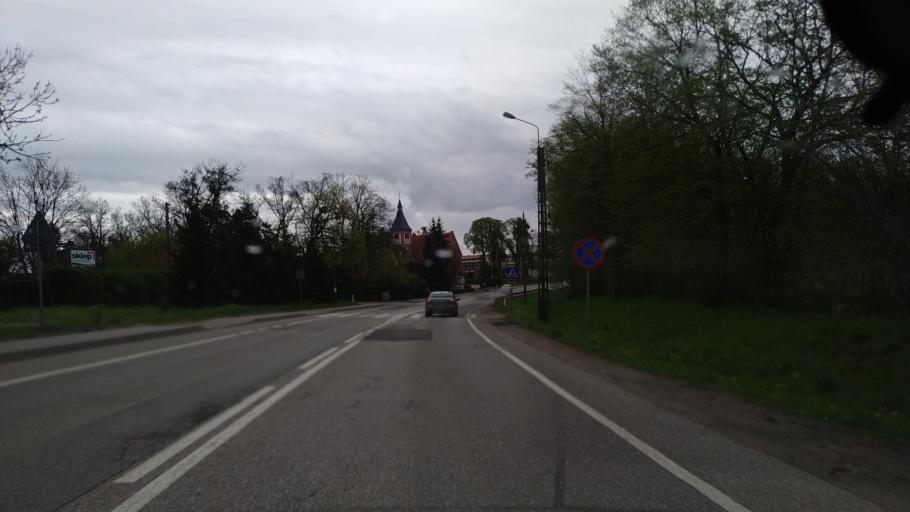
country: PL
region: Pomeranian Voivodeship
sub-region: Powiat tczewski
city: Pelplin
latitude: 54.0366
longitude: 18.6588
